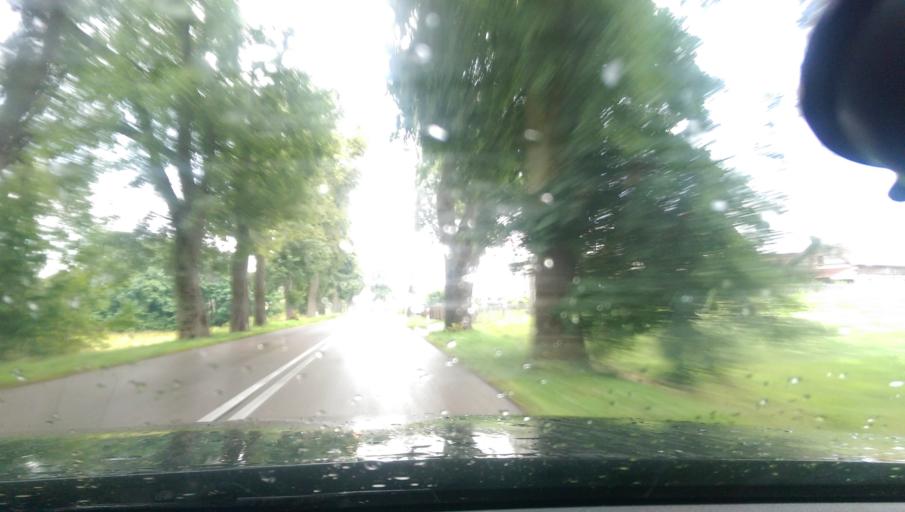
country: PL
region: Warmian-Masurian Voivodeship
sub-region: Powiat piski
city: Ruciane-Nida
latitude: 53.6893
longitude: 21.4867
